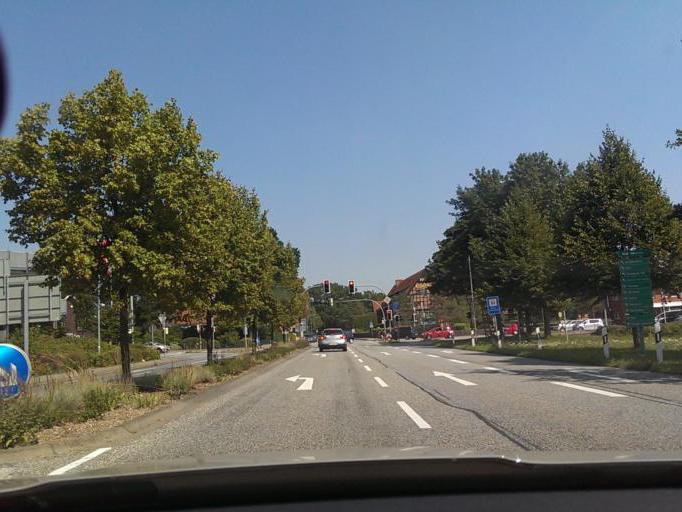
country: DE
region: Lower Saxony
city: Isernhagen Farster Bauerschaft
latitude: 52.4909
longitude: 9.8402
